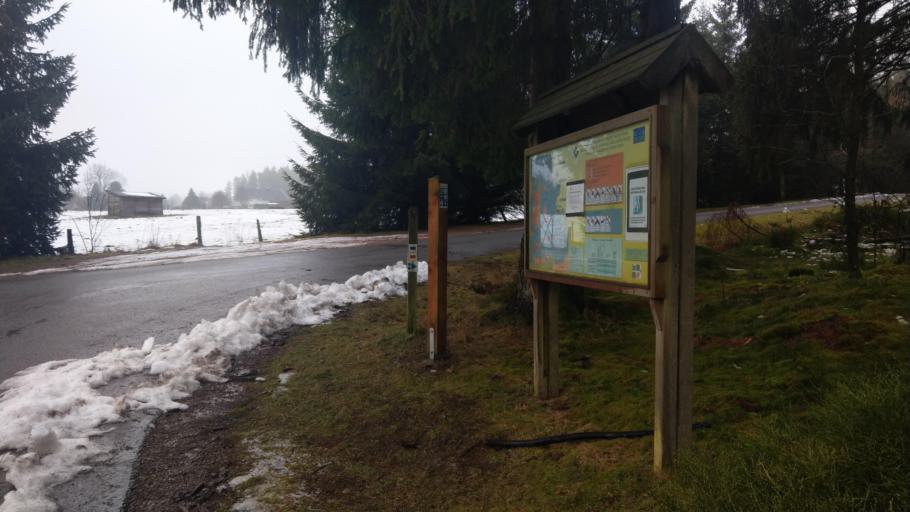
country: DE
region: North Rhine-Westphalia
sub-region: Regierungsbezirk Koln
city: Monschau
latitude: 50.5196
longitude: 6.1942
